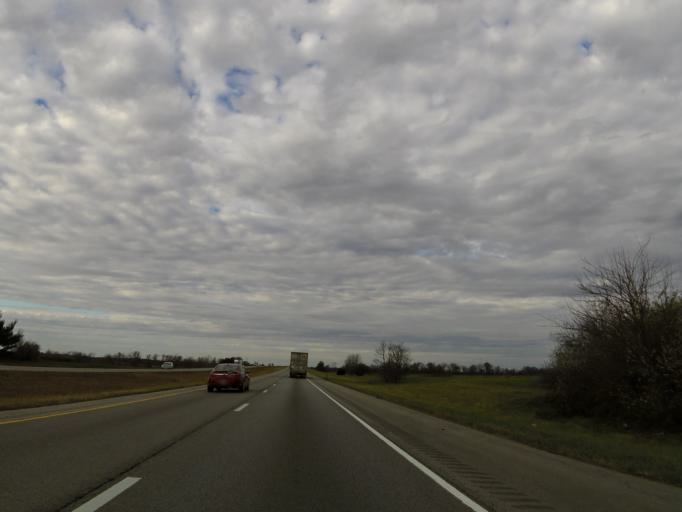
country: US
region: Illinois
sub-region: Clinton County
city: Wamac
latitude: 38.3622
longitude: -89.0631
